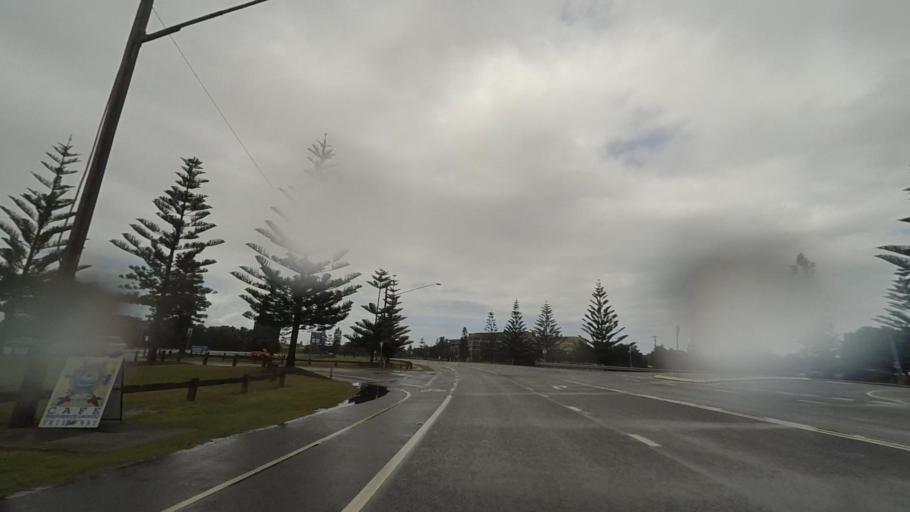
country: AU
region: New South Wales
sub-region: Wyong Shire
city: The Entrance
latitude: -33.3356
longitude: 151.5028
